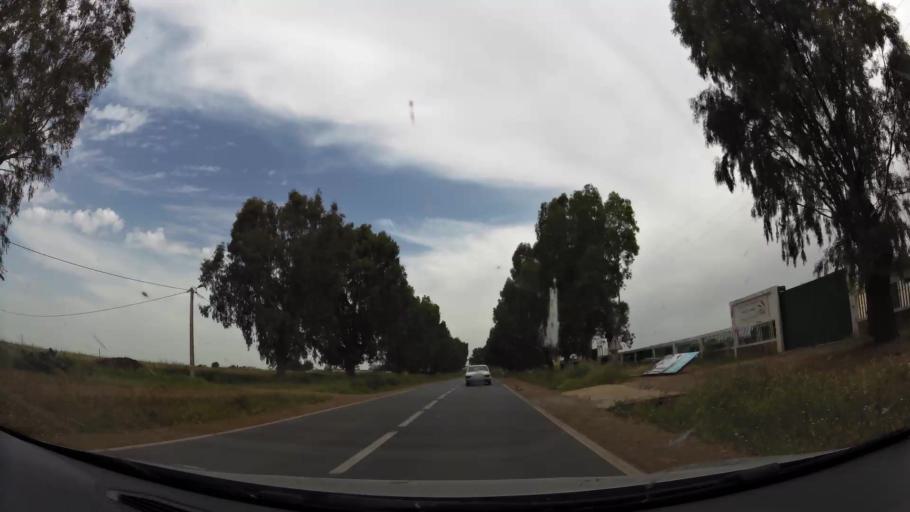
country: MA
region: Rabat-Sale-Zemmour-Zaer
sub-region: Khemisset
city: Tiflet
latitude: 33.8766
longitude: -6.2811
